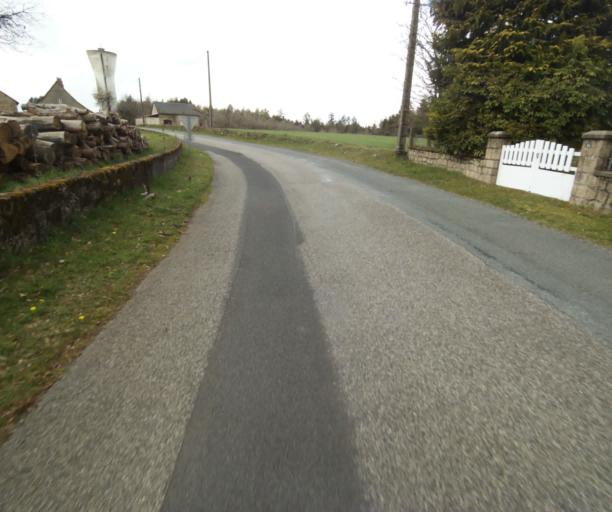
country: FR
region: Limousin
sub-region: Departement de la Correze
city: Correze
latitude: 45.2809
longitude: 1.9762
